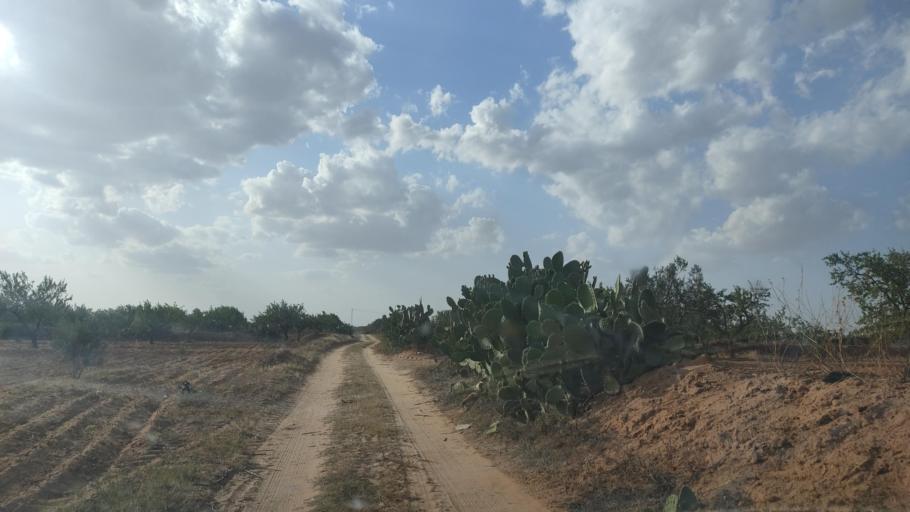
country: TN
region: Safaqis
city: Sfax
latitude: 34.8532
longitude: 10.5922
